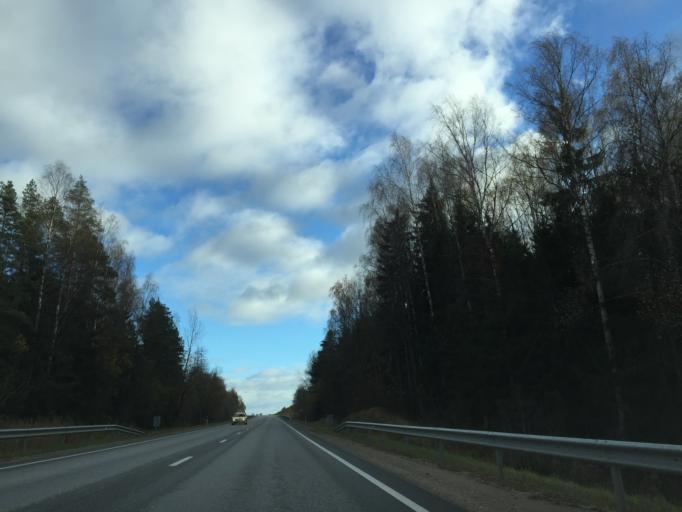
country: LV
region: Tukuma Rajons
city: Tukums
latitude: 56.9862
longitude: 23.0319
